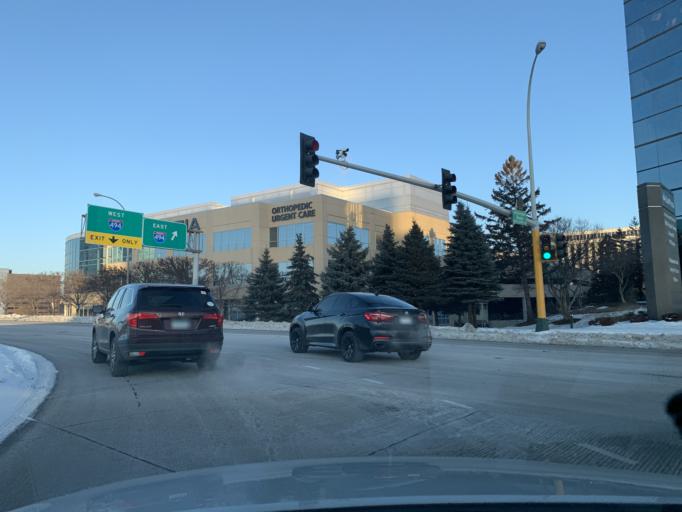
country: US
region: Minnesota
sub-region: Hennepin County
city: Bloomington
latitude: 44.8571
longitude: -93.3287
